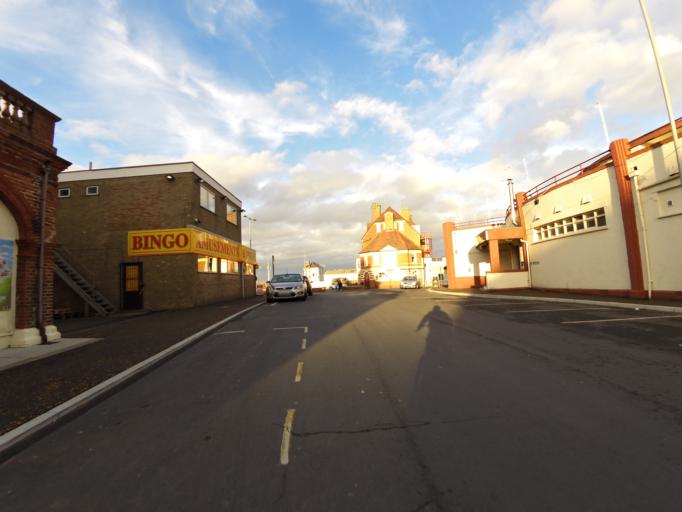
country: GB
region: England
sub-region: Norfolk
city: Gorleston-on-Sea
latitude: 52.5709
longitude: 1.7328
